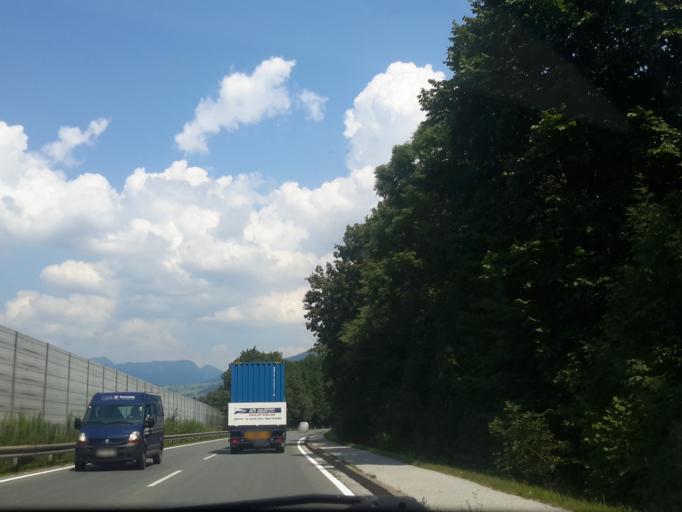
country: AT
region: Tyrol
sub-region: Politischer Bezirk Kufstein
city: Kufstein
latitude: 47.5915
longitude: 12.1674
